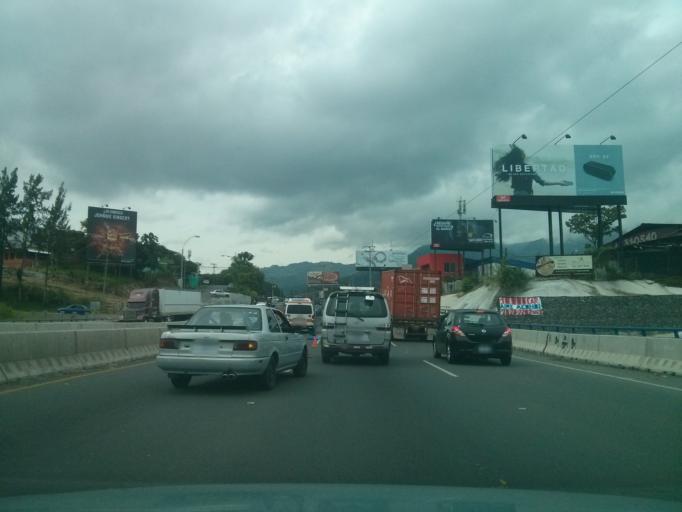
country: CR
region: San Jose
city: San Rafael
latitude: 9.9307
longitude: -84.1164
